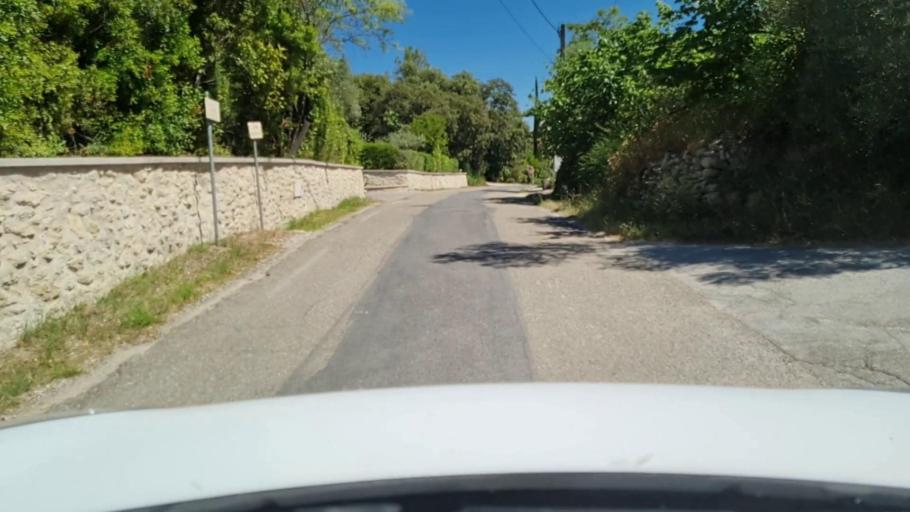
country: FR
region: Languedoc-Roussillon
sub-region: Departement du Gard
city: Villevieille
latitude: 43.7950
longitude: 4.1007
